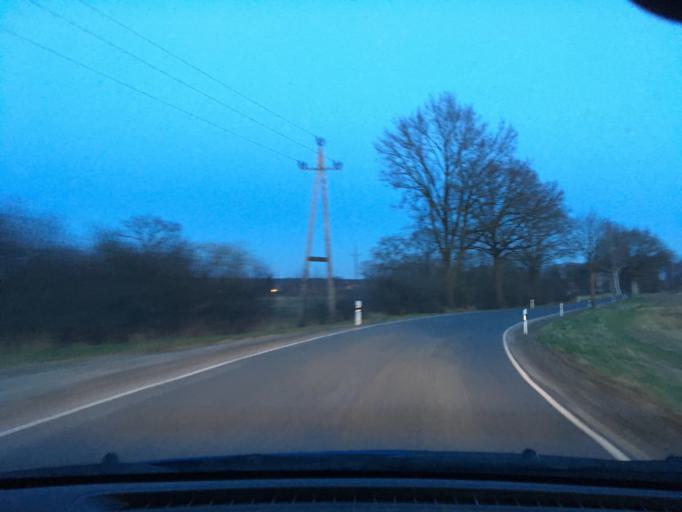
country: DE
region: Lower Saxony
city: Eyendorf
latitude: 53.2003
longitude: 10.1899
